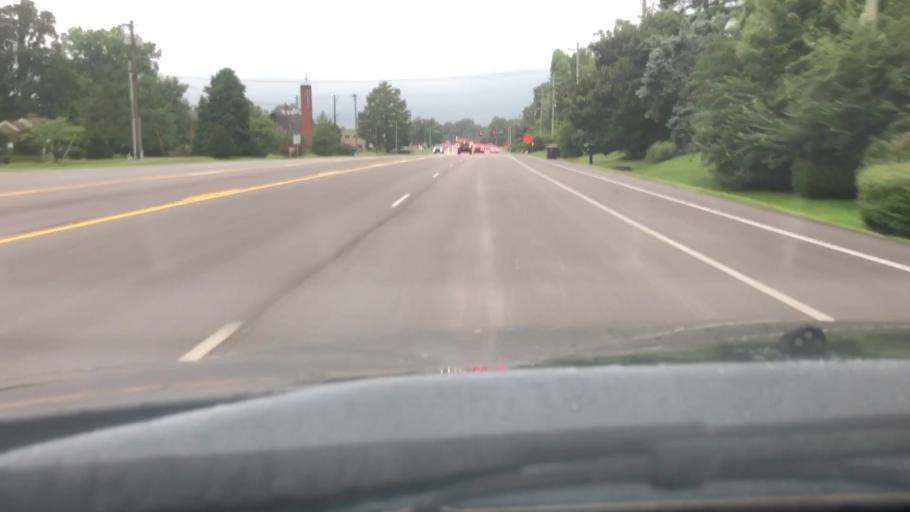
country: US
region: Kentucky
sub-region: Jefferson County
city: Hurstbourne Acres
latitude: 38.2095
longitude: -85.5849
